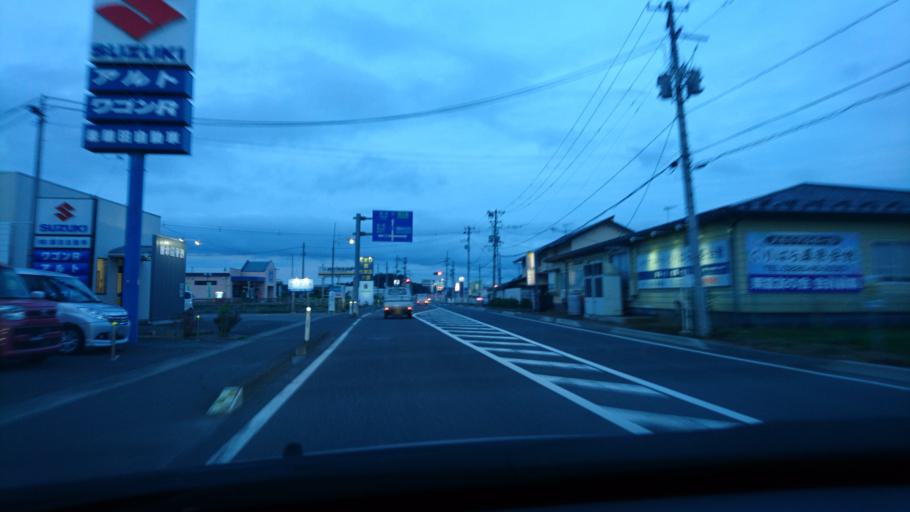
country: JP
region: Iwate
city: Ichinoseki
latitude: 38.8317
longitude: 140.9979
